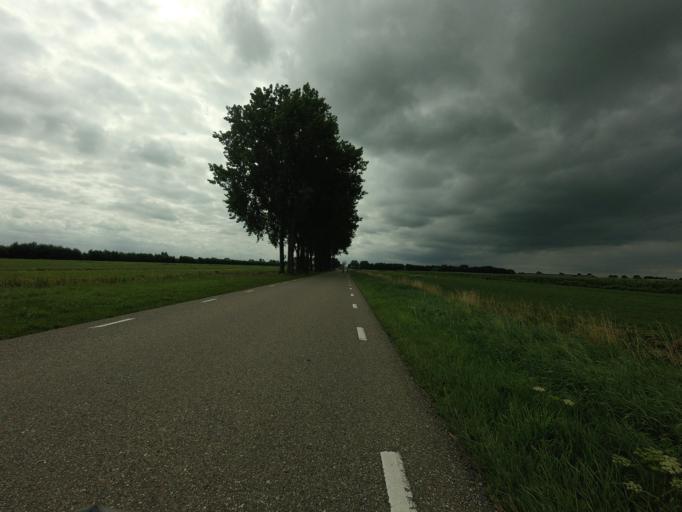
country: NL
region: Utrecht
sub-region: Gemeente Lopik
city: Lopik
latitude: 51.9310
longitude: 4.9112
